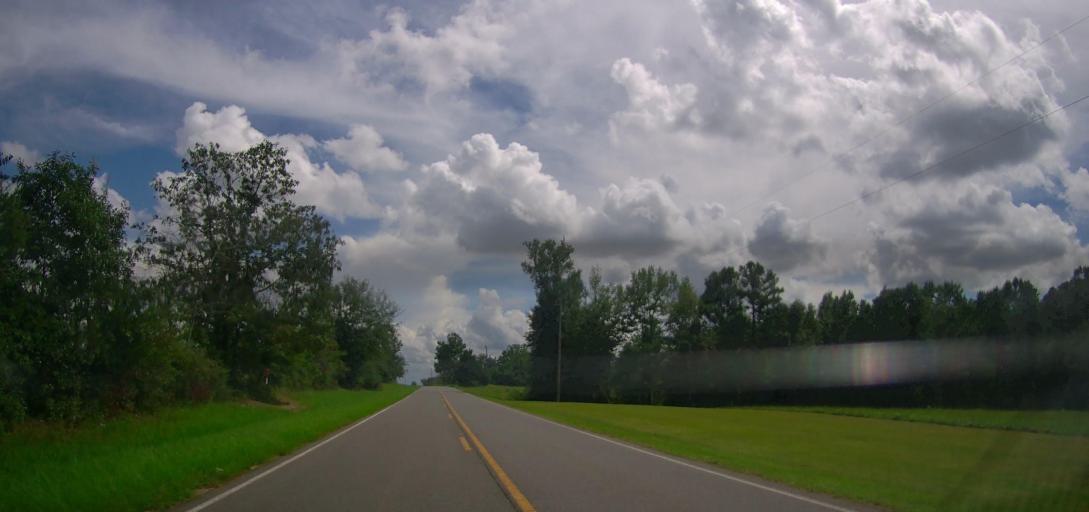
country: US
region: Georgia
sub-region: Taylor County
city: Butler
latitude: 32.4754
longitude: -84.2042
